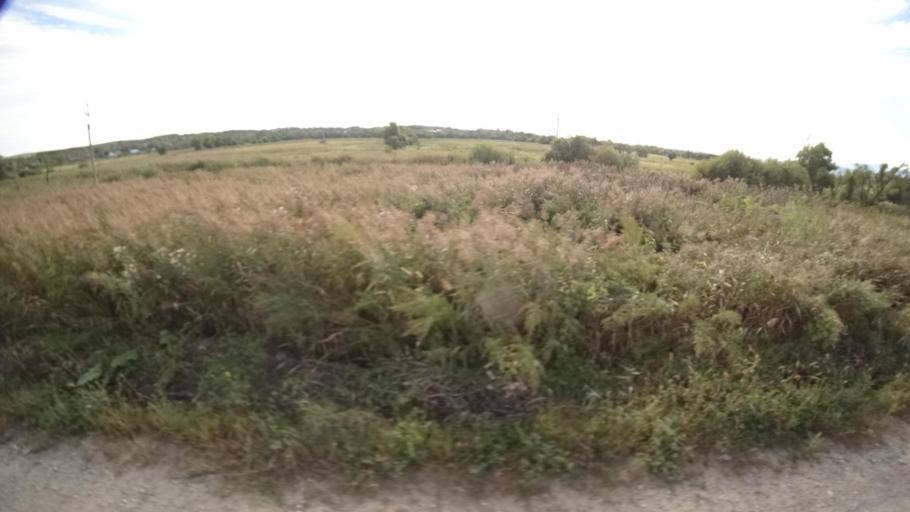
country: RU
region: Primorskiy
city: Dostoyevka
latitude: 44.3114
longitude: 133.4632
